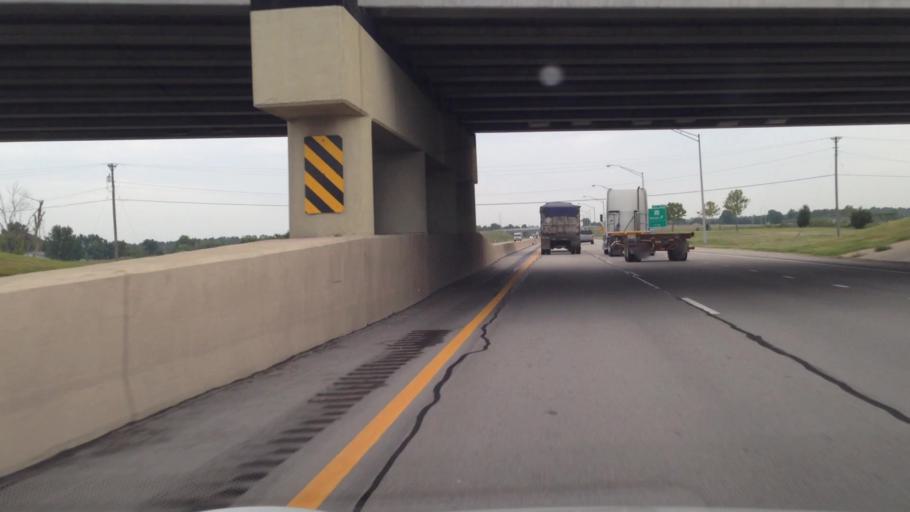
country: US
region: Oklahoma
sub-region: Ottawa County
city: Miami
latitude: 36.8712
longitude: -94.8473
